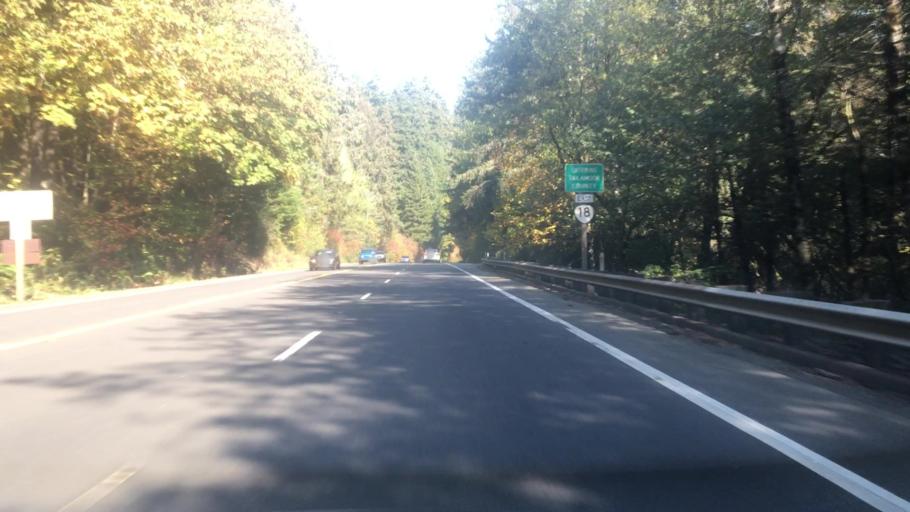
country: US
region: Oregon
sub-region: Lincoln County
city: Rose Lodge
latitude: 45.0447
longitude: -123.8018
